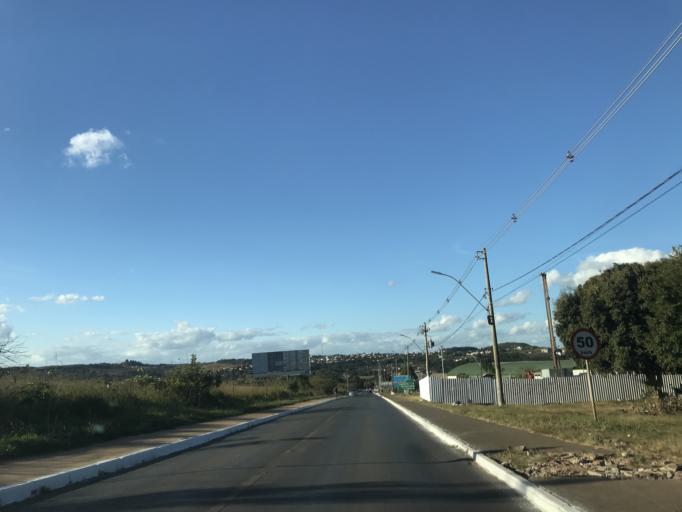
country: BR
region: Federal District
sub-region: Brasilia
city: Brasilia
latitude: -15.8931
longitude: -47.7838
